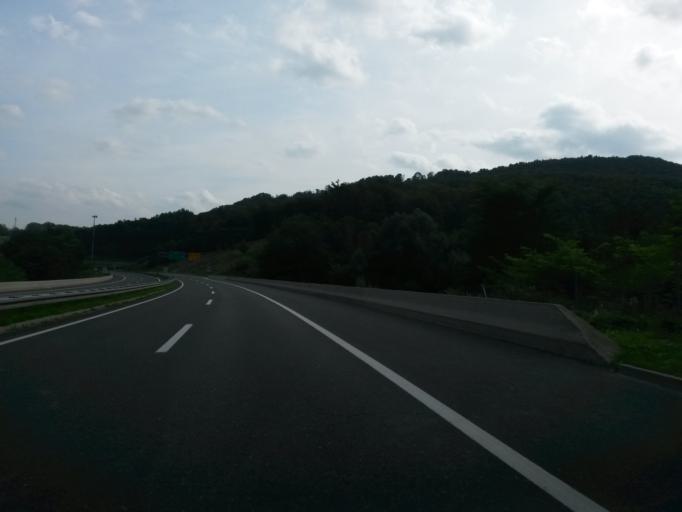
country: HR
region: Varazdinska
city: Ljubescica
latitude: 46.2133
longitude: 16.4044
